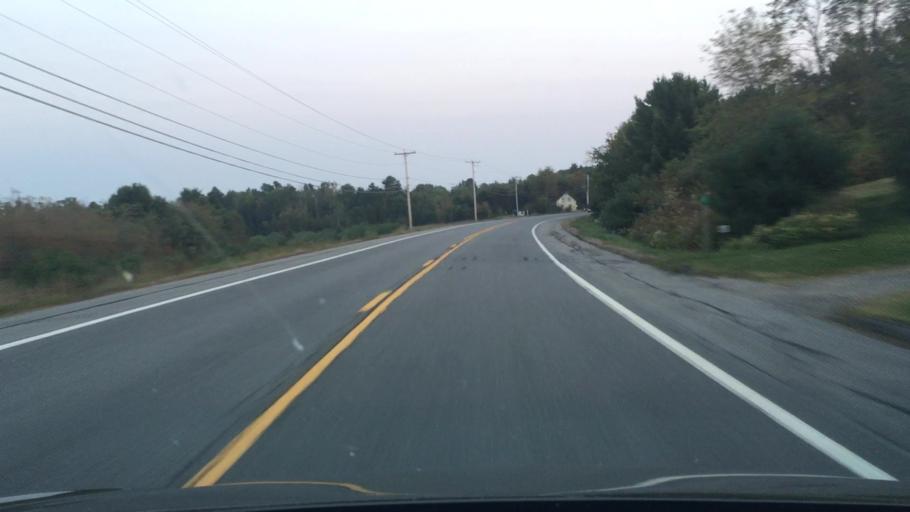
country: US
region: Maine
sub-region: Waldo County
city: Stockton Springs
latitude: 44.5391
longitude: -68.8613
